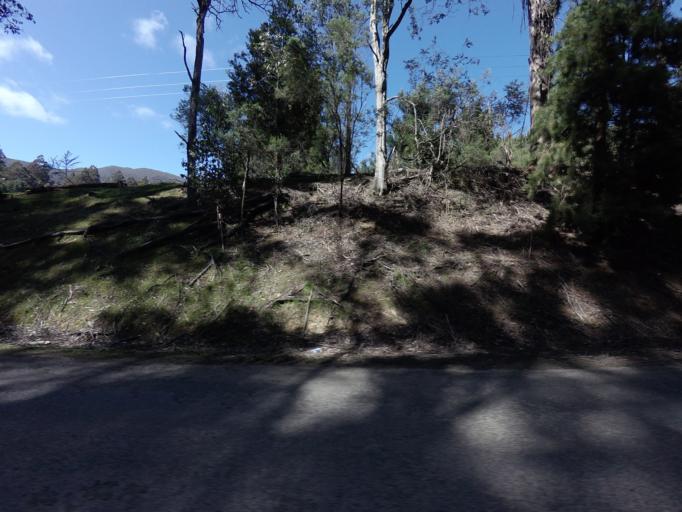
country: AU
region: Tasmania
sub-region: Derwent Valley
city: New Norfolk
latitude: -42.7595
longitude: 146.6132
